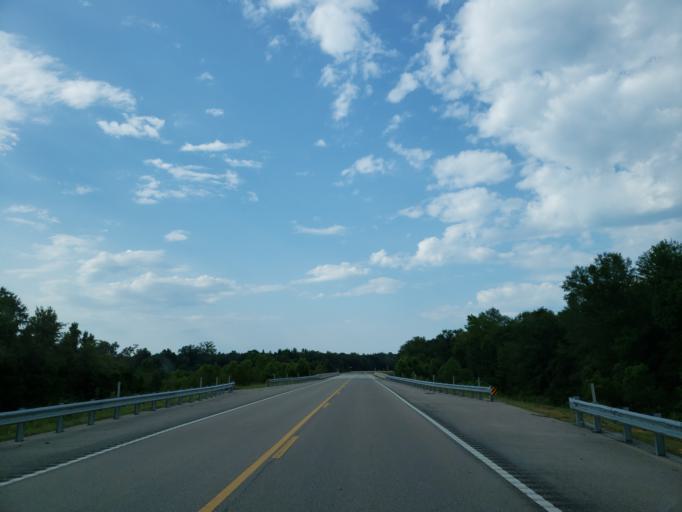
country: US
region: Mississippi
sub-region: Clarke County
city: Stonewall
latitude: 32.1713
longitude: -88.9302
